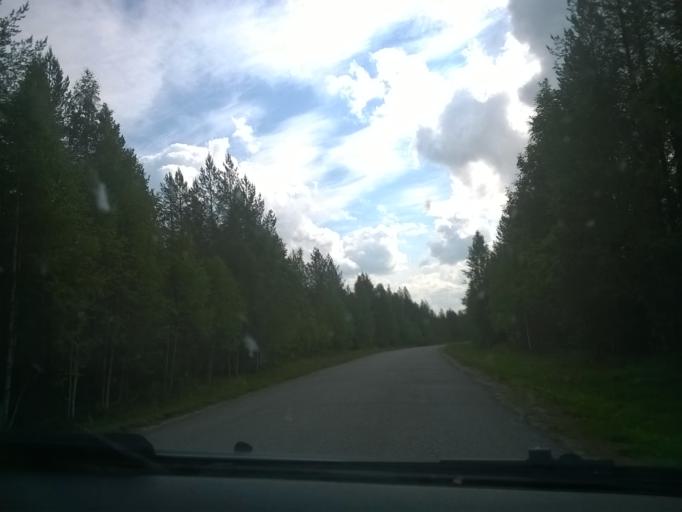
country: FI
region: Kainuu
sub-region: Kehys-Kainuu
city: Kuhmo
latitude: 64.4479
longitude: 29.6935
